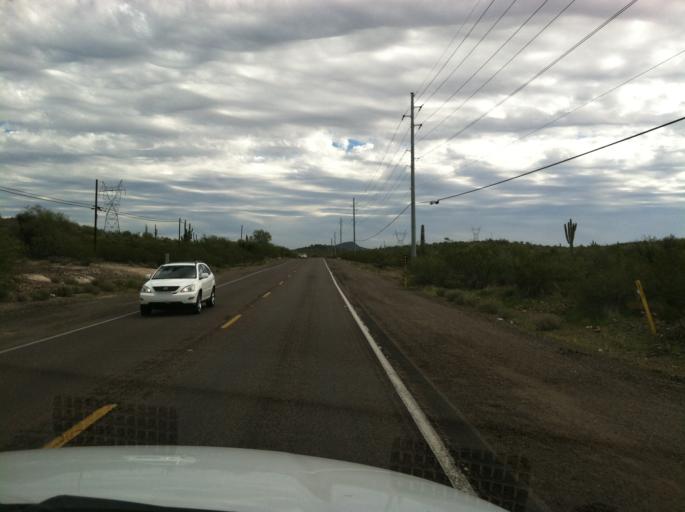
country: US
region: Arizona
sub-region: Maricopa County
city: New River
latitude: 33.9208
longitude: -112.1059
